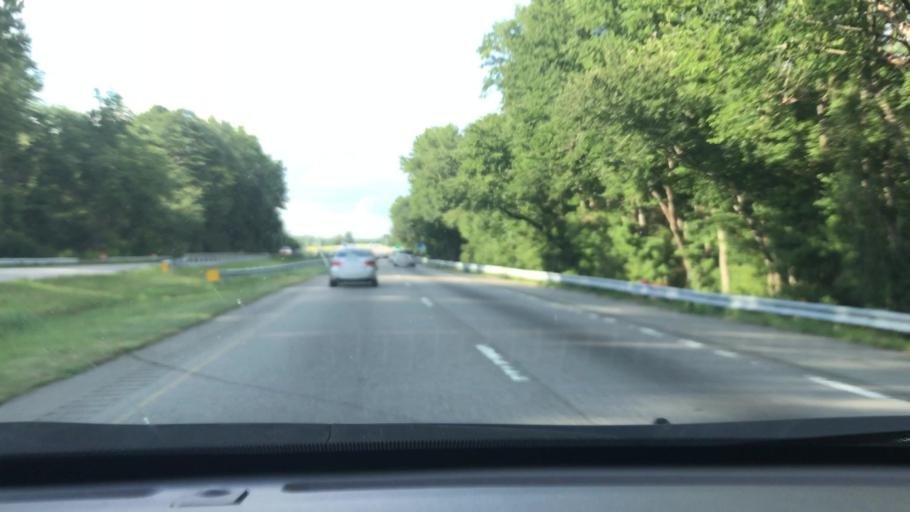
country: US
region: North Carolina
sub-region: Robeson County
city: Saint Pauls
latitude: 34.8021
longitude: -78.9901
